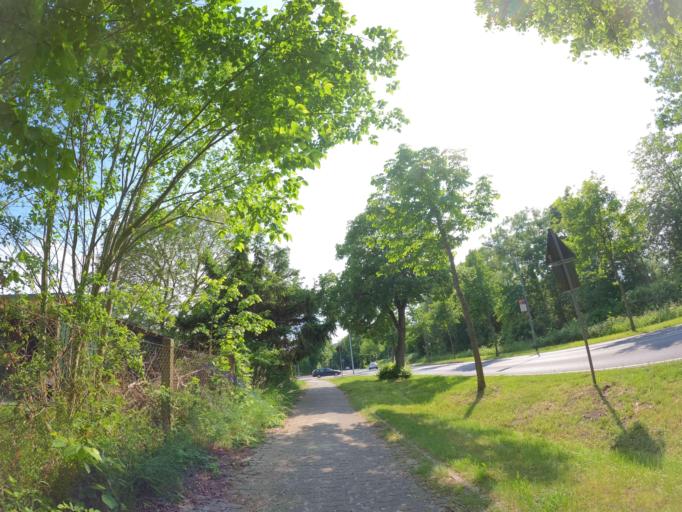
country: DE
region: Mecklenburg-Vorpommern
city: Stralsund
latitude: 54.2898
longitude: 13.0532
